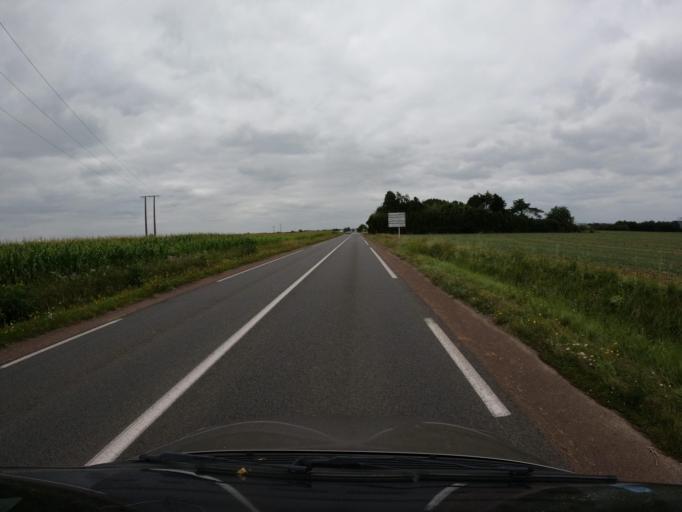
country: FR
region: Pays de la Loire
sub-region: Departement de la Vendee
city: Saint-Hilaire-des-Loges
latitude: 46.4046
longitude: -0.6752
